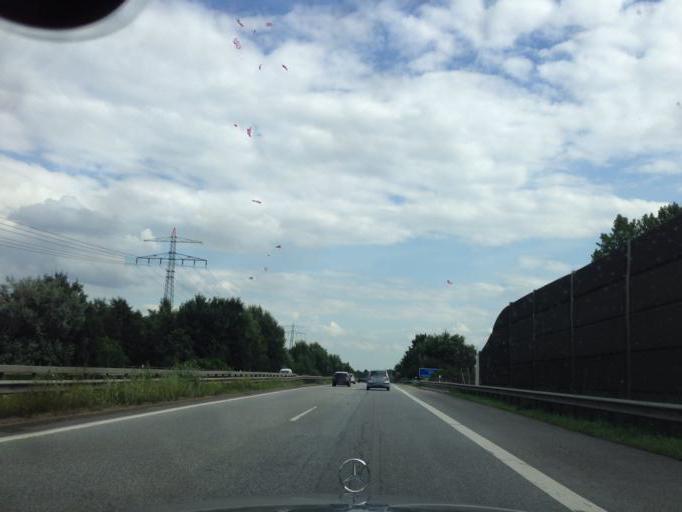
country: DE
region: Hamburg
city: Rothenburgsort
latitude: 53.4974
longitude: 10.0944
